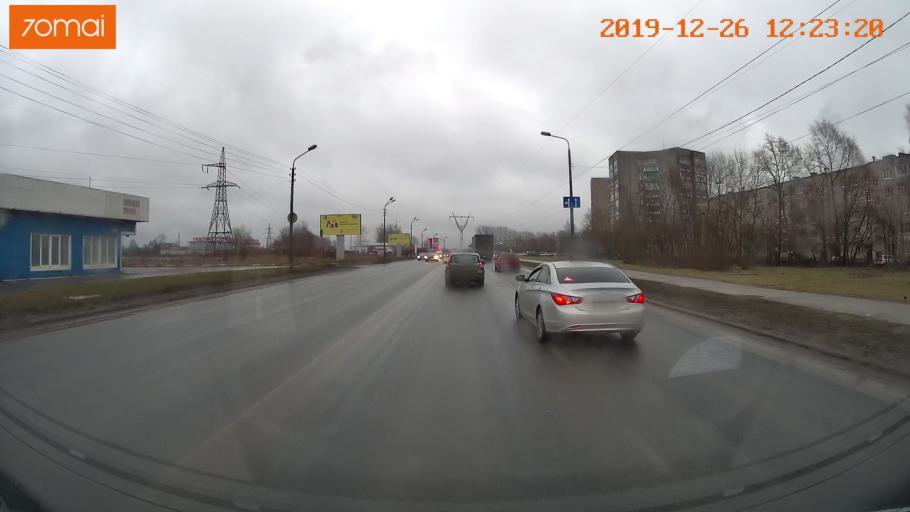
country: RU
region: Vologda
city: Tonshalovo
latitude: 59.1496
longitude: 37.9567
